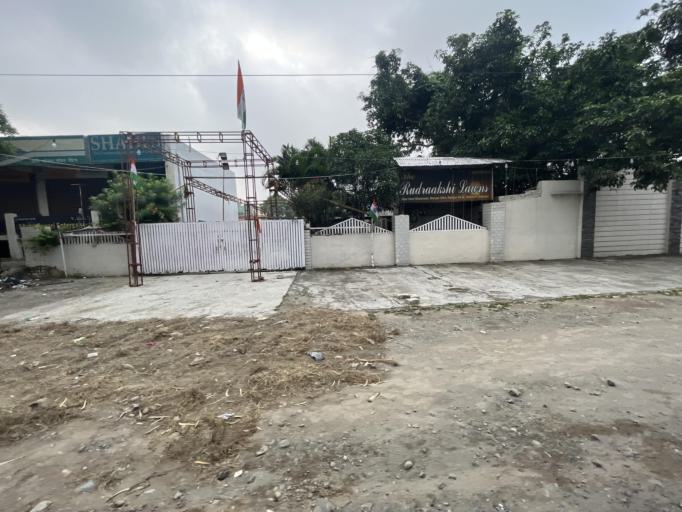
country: IN
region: Uttarakhand
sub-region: Naini Tal
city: Haldwani
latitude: 29.1989
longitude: 79.5136
